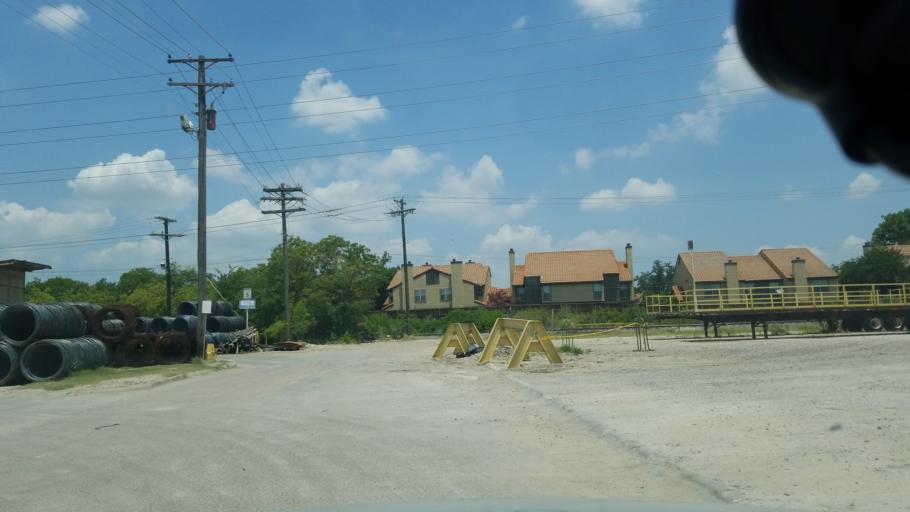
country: US
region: Texas
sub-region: Dallas County
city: Carrollton
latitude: 32.9588
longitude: -96.8641
